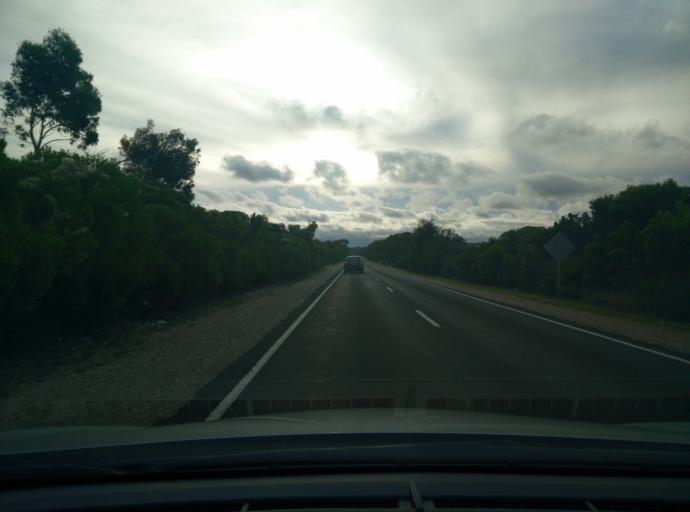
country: AU
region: South Australia
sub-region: Kangaroo Island
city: Kingscote
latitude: -35.8367
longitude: 137.7854
